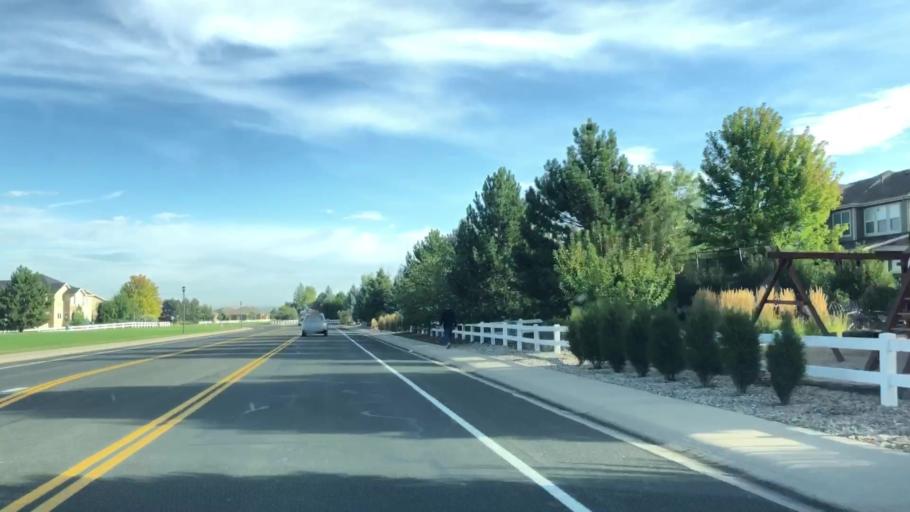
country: US
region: Colorado
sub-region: Weld County
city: Windsor
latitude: 40.4658
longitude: -104.9769
